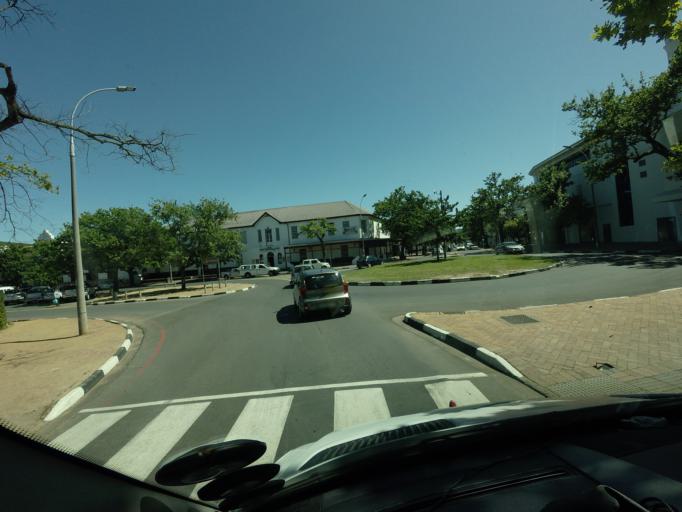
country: ZA
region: Western Cape
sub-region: Cape Winelands District Municipality
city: Stellenbosch
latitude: -33.9363
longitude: 18.8591
